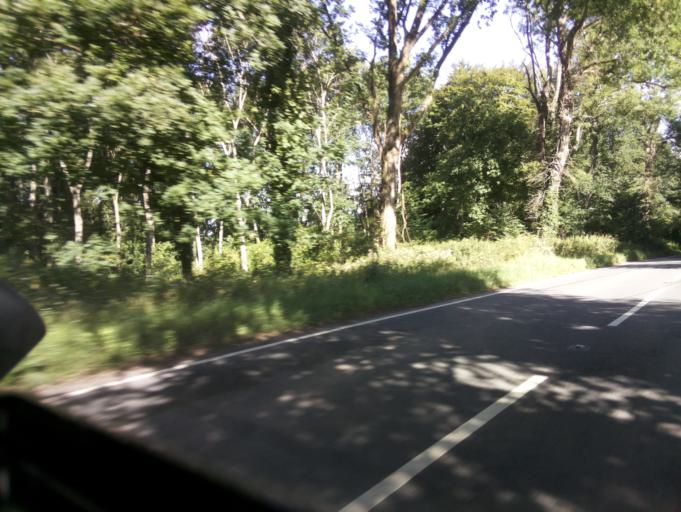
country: GB
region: England
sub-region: Herefordshire
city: Yatton
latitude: 51.9703
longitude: -2.5522
